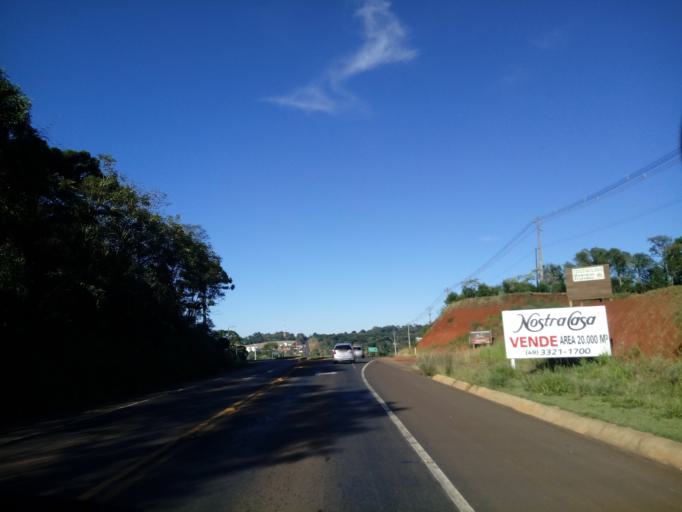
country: BR
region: Santa Catarina
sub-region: Chapeco
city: Chapeco
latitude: -27.1628
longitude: -52.6302
